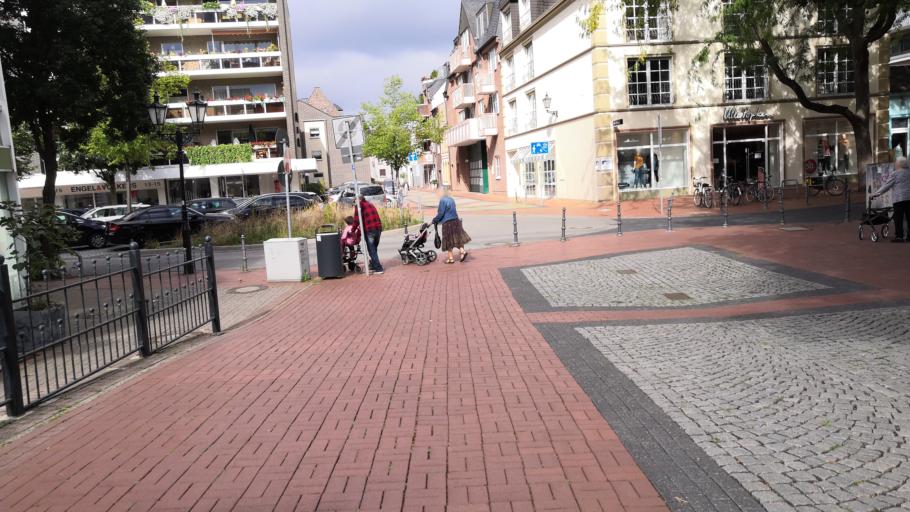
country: DE
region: North Rhine-Westphalia
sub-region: Regierungsbezirk Dusseldorf
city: Moers
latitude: 51.4511
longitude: 6.6250
